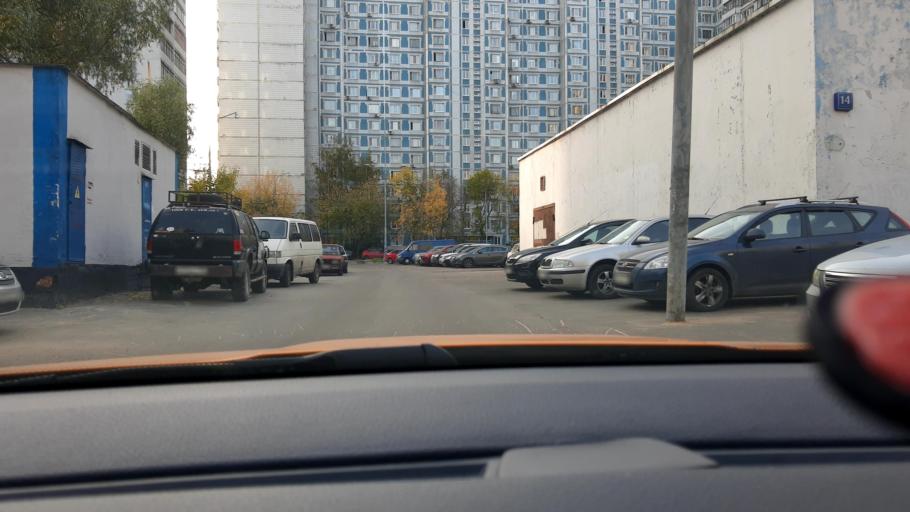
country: RU
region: Moskovskaya
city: Levoberezhnaya
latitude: 55.8829
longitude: 37.4887
